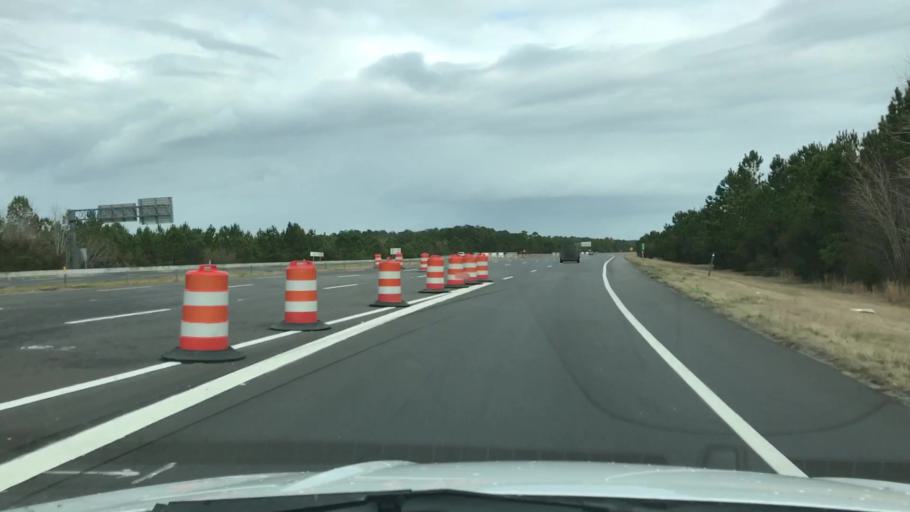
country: US
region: South Carolina
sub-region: Horry County
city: Socastee
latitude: 33.7047
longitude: -79.0127
